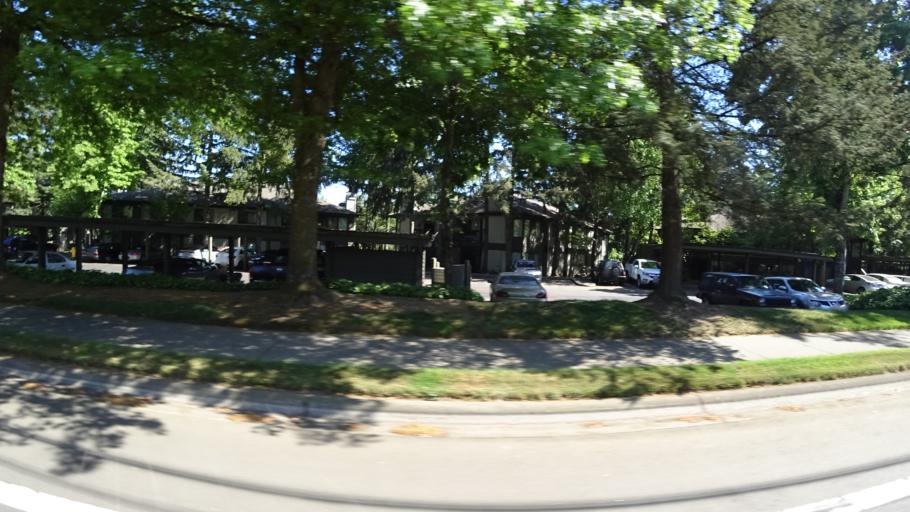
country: US
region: Oregon
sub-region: Washington County
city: Rockcreek
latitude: 45.5341
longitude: -122.8629
